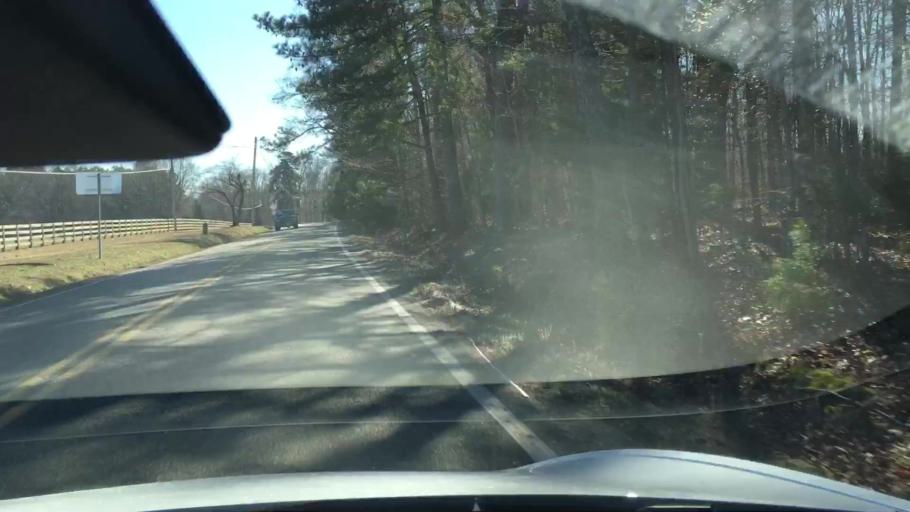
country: US
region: Virginia
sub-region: Henrico County
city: Short Pump
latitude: 37.5678
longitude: -77.7110
